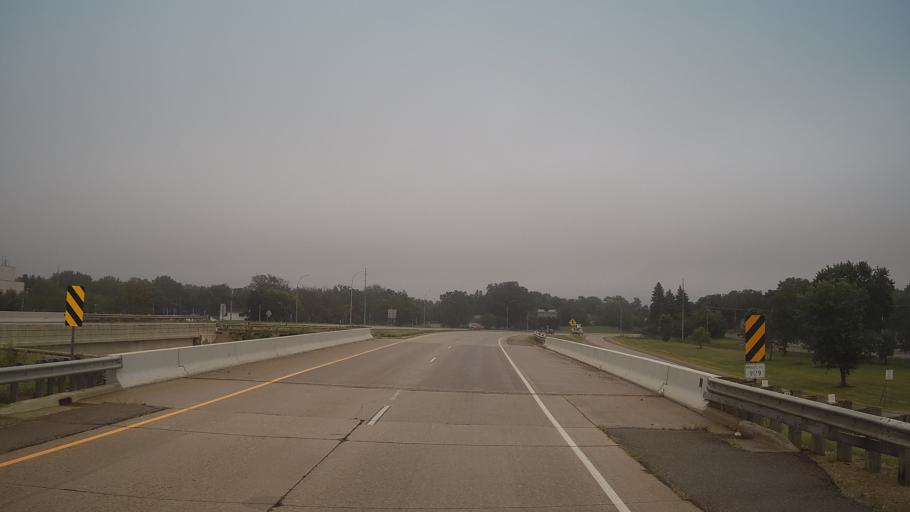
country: US
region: Minnesota
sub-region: Mower County
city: Austin
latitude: 43.6805
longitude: -92.9678
